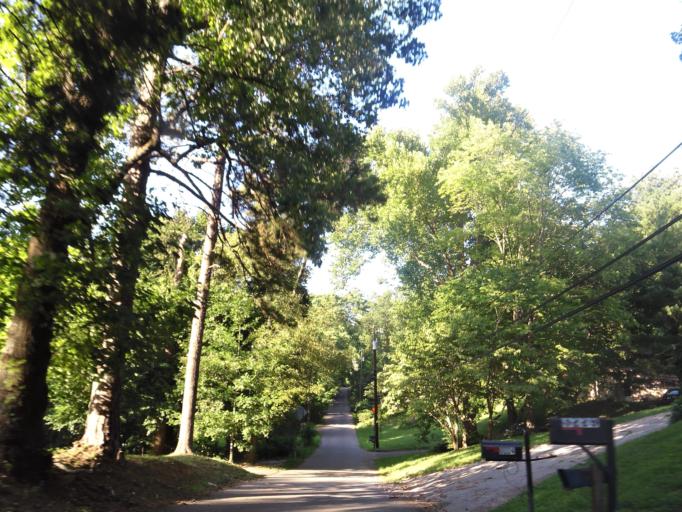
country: US
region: Tennessee
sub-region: Knox County
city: Knoxville
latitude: 35.9093
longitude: -83.9523
